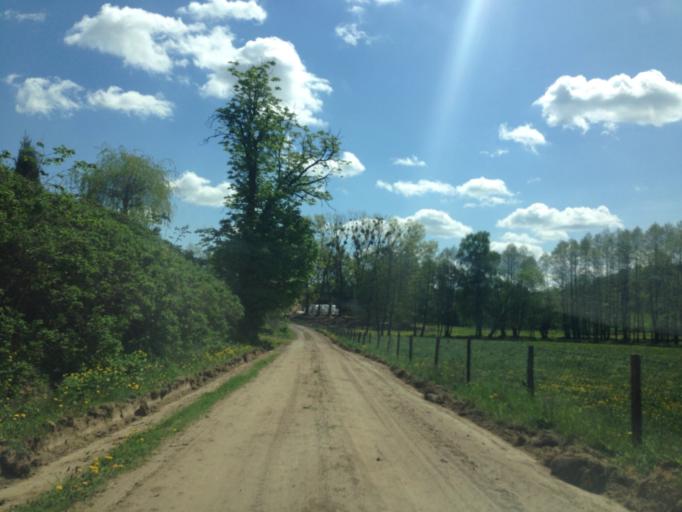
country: PL
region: Kujawsko-Pomorskie
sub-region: Powiat brodnicki
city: Brzozie
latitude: 53.3054
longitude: 19.6479
